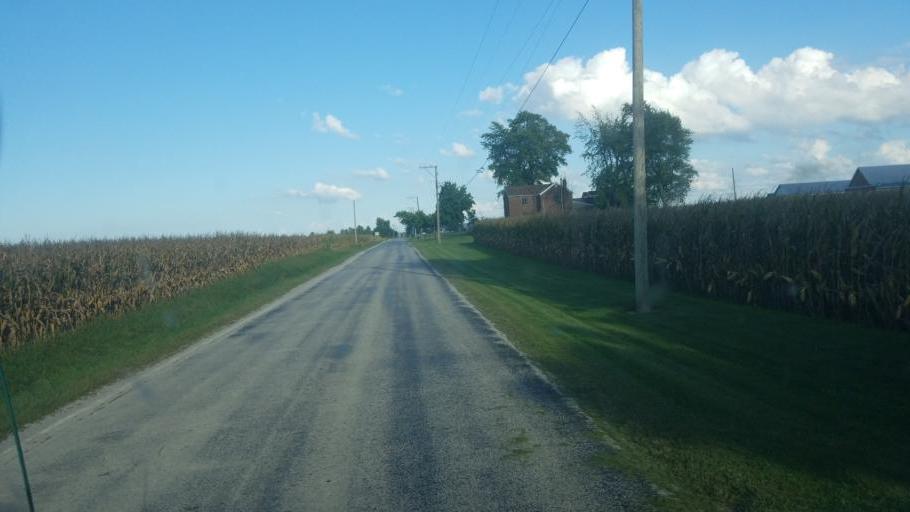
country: US
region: Ohio
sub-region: Hancock County
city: Arlington
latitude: 40.9356
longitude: -83.6172
